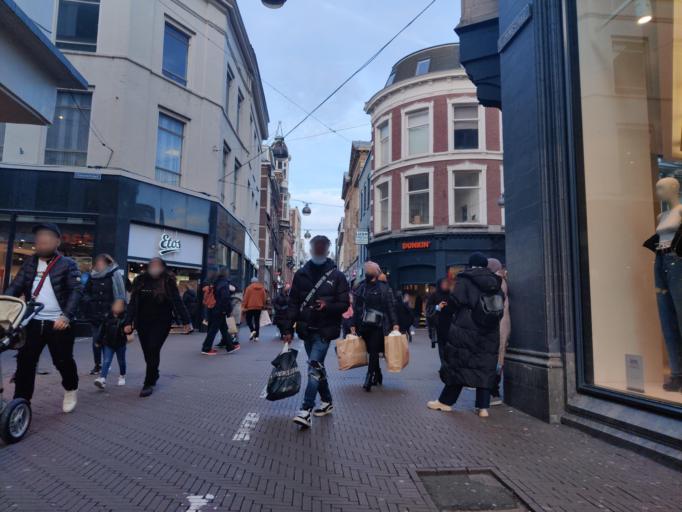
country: NL
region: South Holland
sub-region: Gemeente Den Haag
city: The Hague
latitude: 52.0769
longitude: 4.3103
